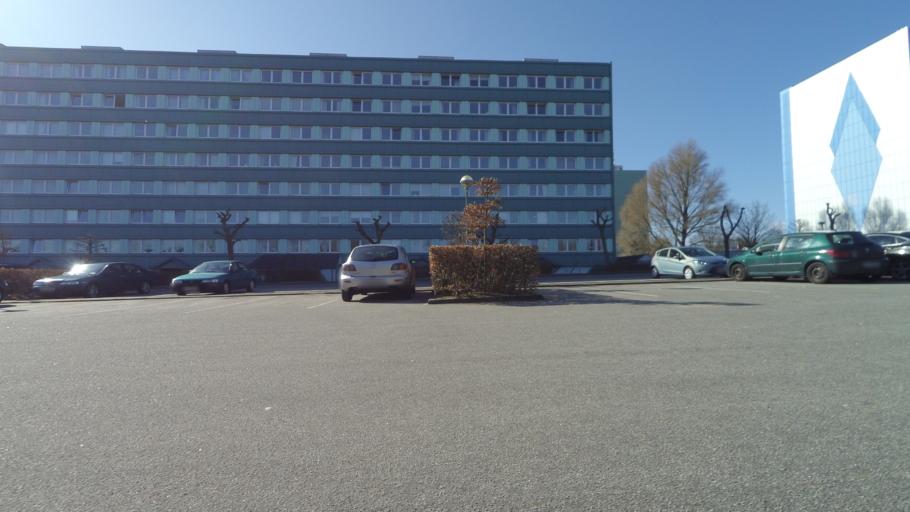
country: DK
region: Central Jutland
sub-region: Arhus Kommune
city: Arhus
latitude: 56.1701
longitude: 10.1755
